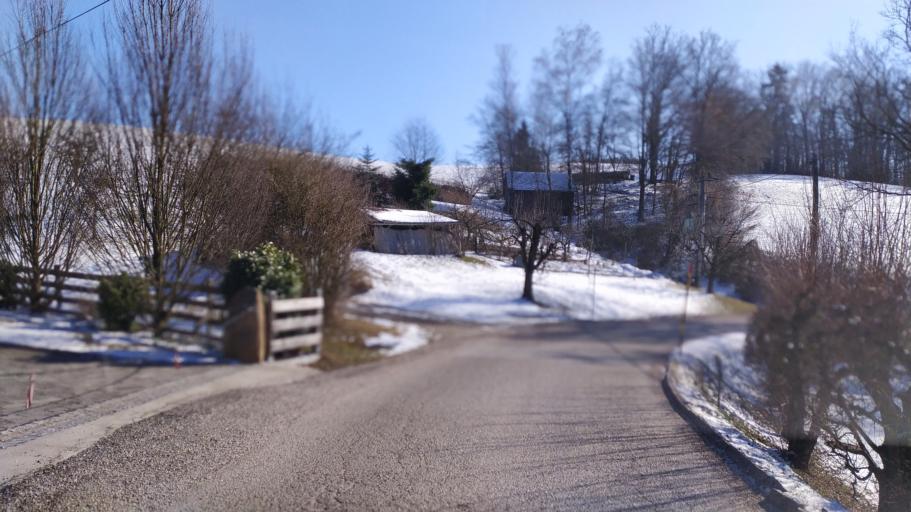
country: AT
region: Upper Austria
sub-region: Politischer Bezirk Urfahr-Umgebung
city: Ottensheim
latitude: 48.3445
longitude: 14.1940
